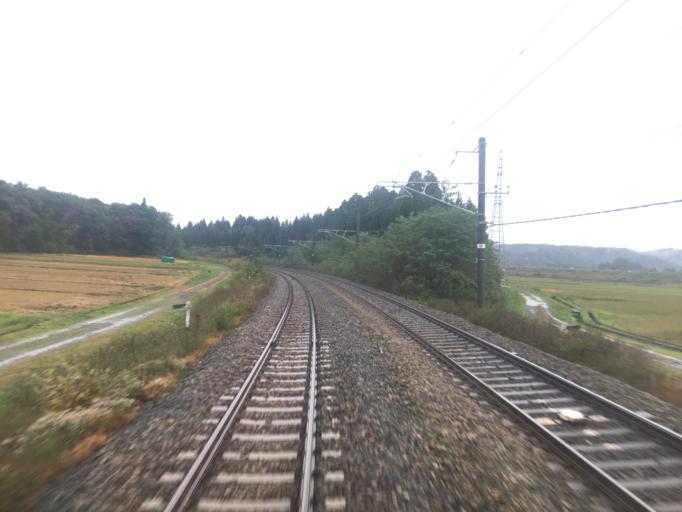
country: JP
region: Yamagata
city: Shinjo
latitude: 38.7353
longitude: 140.3068
